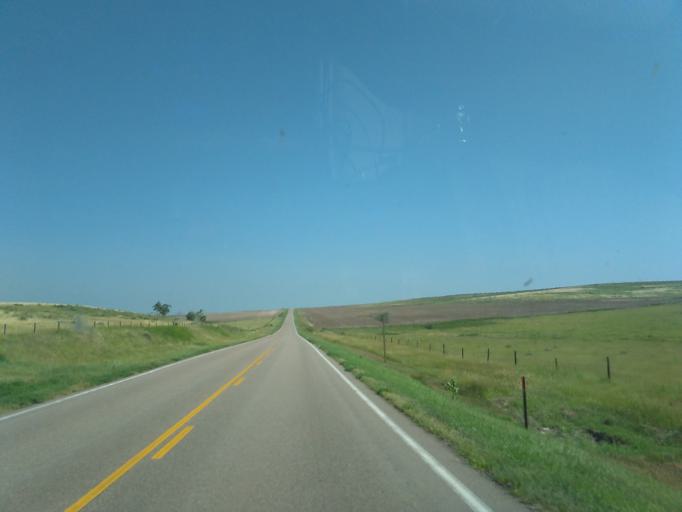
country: US
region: Nebraska
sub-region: Dundy County
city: Benkelman
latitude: 39.9606
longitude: -101.5416
